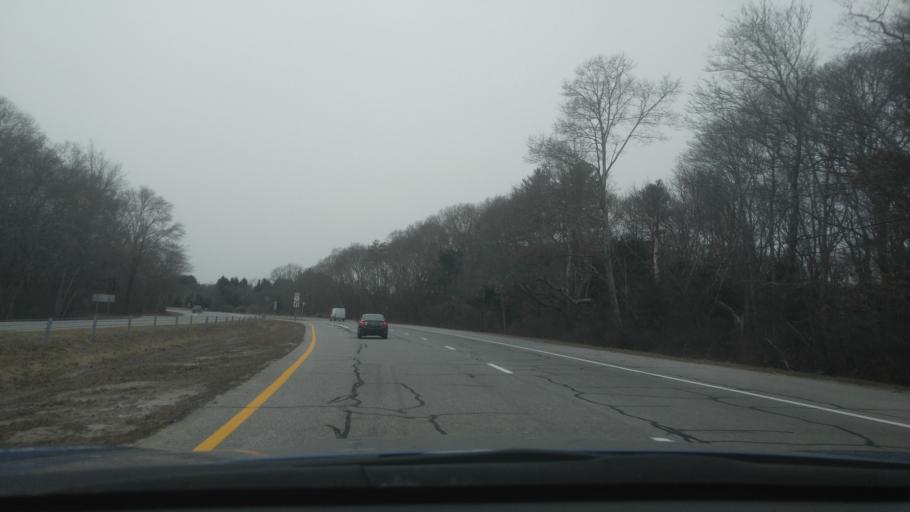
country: US
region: Rhode Island
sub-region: Washington County
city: Wakefield-Peacedale
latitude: 41.4264
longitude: -71.5225
